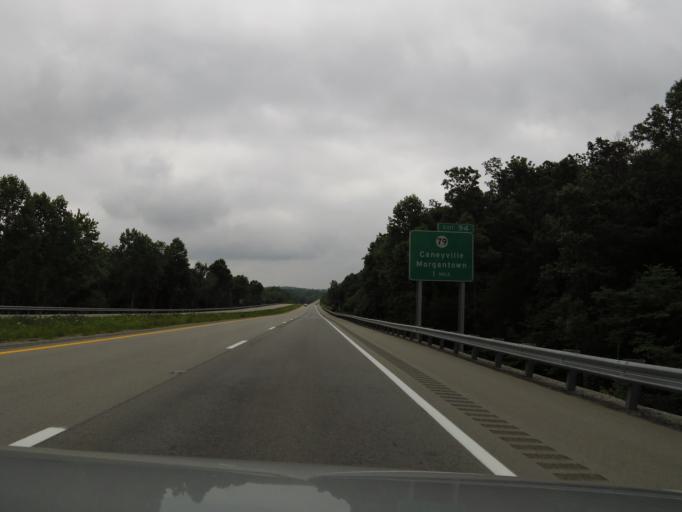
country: US
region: Kentucky
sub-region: Ohio County
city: Oak Grove
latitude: 37.4114
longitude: -86.5270
